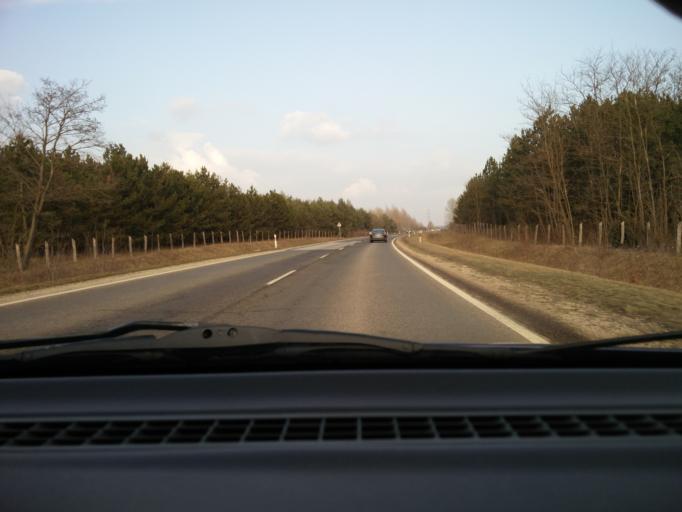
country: HU
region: Pest
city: Ujhartyan
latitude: 47.2350
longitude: 19.4249
